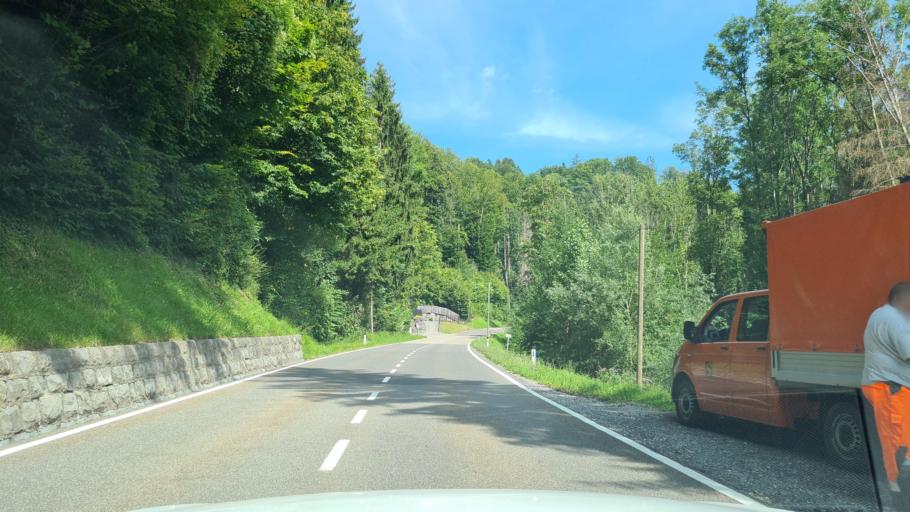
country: AT
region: Vorarlberg
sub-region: Politischer Bezirk Bregenz
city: Bildstein
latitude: 47.4457
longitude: 9.7744
